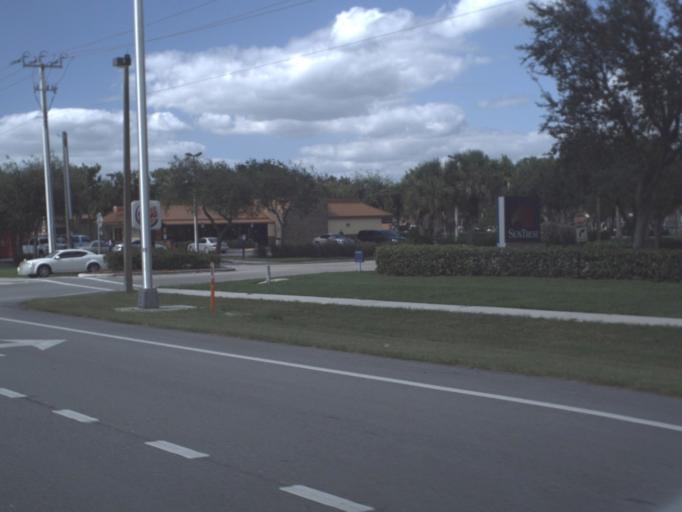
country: US
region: Florida
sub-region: Collier County
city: Lely Resort
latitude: 26.0641
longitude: -81.7002
